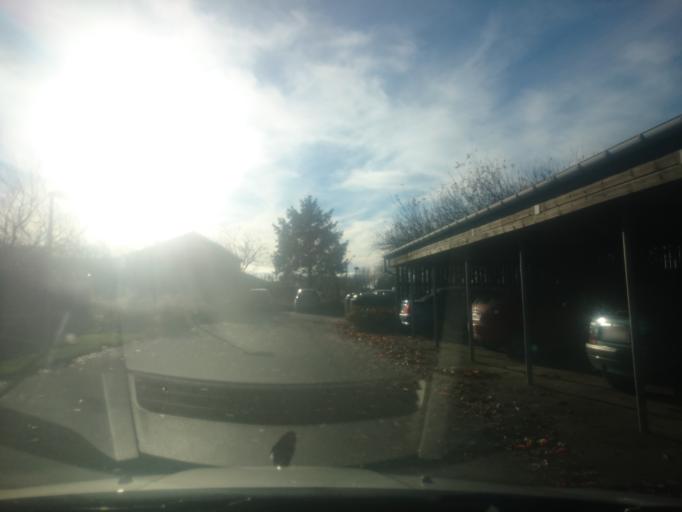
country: DK
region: South Denmark
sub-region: Billund Kommune
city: Billund
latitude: 55.7291
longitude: 9.1044
